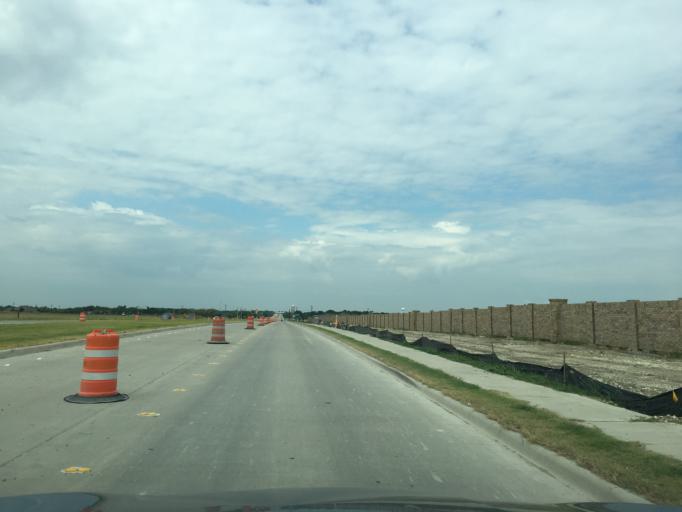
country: US
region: Texas
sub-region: Collin County
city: Melissa
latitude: 33.2951
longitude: -96.5419
